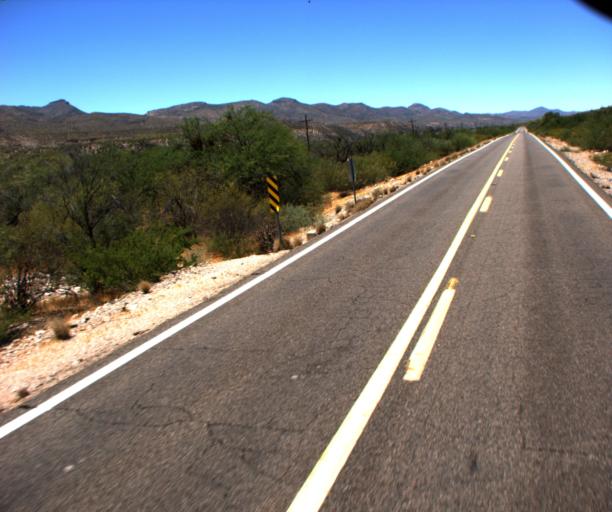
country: US
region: Arizona
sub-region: Pinal County
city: Kearny
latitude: 33.1033
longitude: -110.7481
